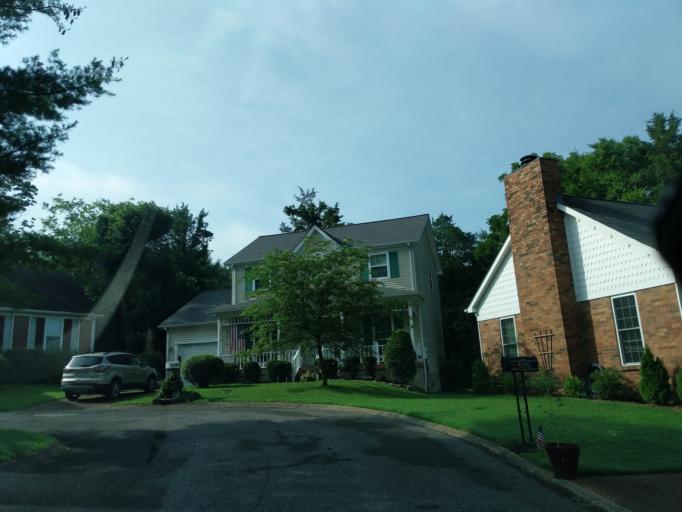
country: US
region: Tennessee
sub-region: Davidson County
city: Goodlettsville
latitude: 36.3141
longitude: -86.6918
